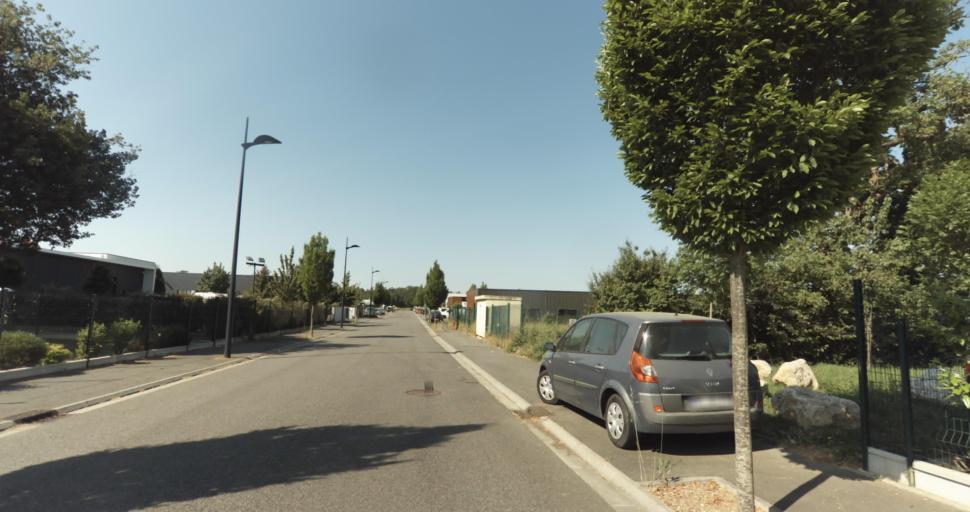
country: FR
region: Midi-Pyrenees
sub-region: Departement de la Haute-Garonne
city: La Salvetat-Saint-Gilles
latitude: 43.5956
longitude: 1.2867
